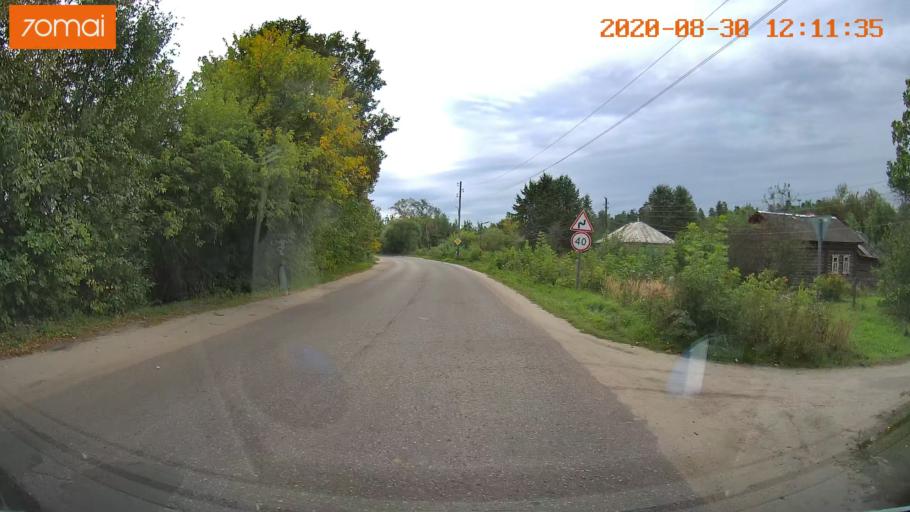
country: RU
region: Ivanovo
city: Yur'yevets
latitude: 57.3131
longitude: 43.0957
